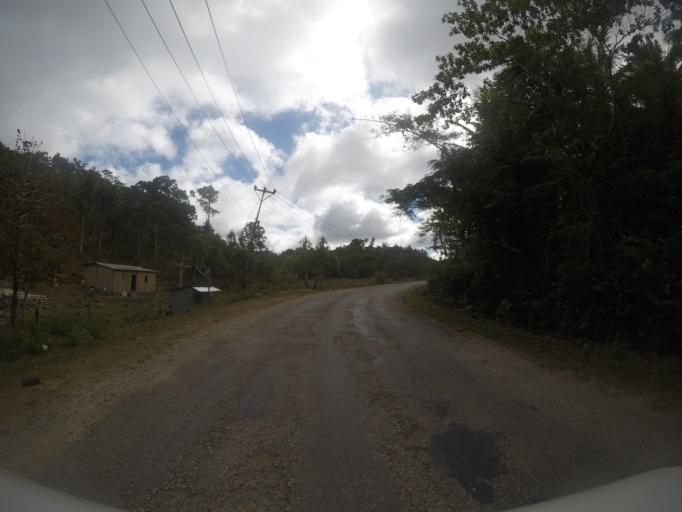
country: TL
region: Lautem
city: Lospalos
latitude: -8.5422
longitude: 126.9512
